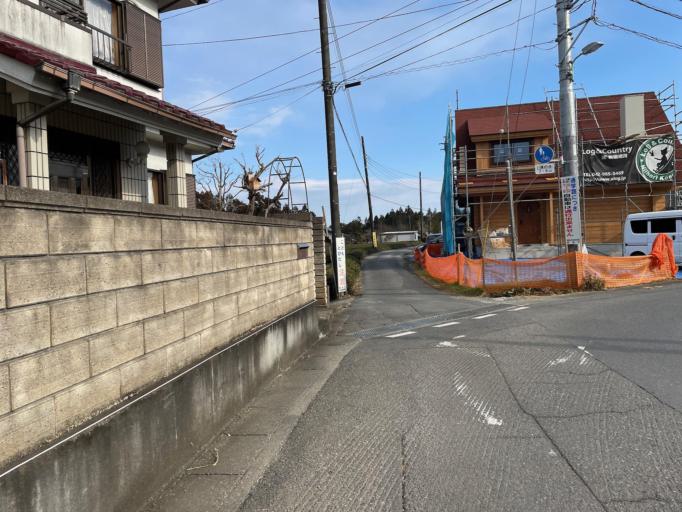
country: JP
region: Saitama
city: Hanno
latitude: 35.8384
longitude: 139.3062
